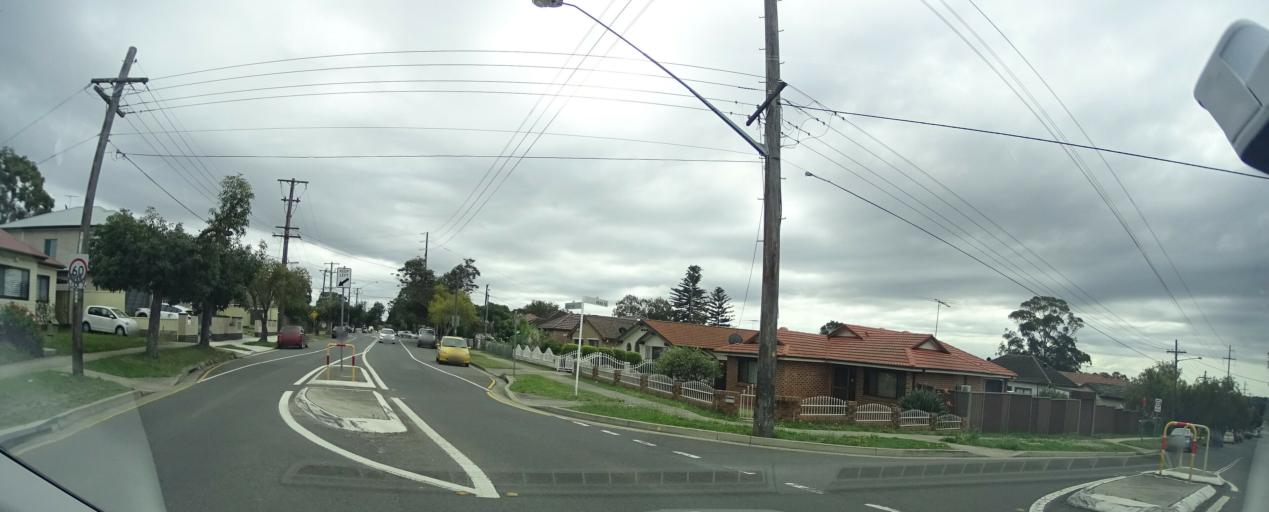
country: AU
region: New South Wales
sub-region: Bankstown
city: Padstow
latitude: -33.9519
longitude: 151.0263
